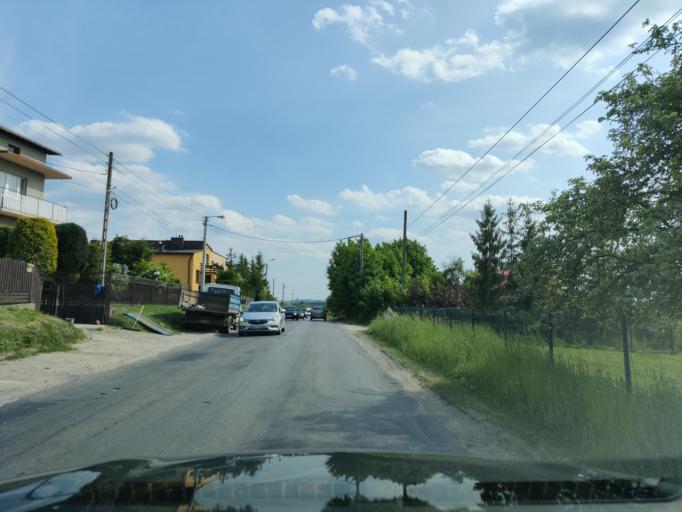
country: PL
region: Silesian Voivodeship
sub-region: Dabrowa Gornicza
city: Dabrowa Gornicza
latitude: 50.3877
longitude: 19.2421
